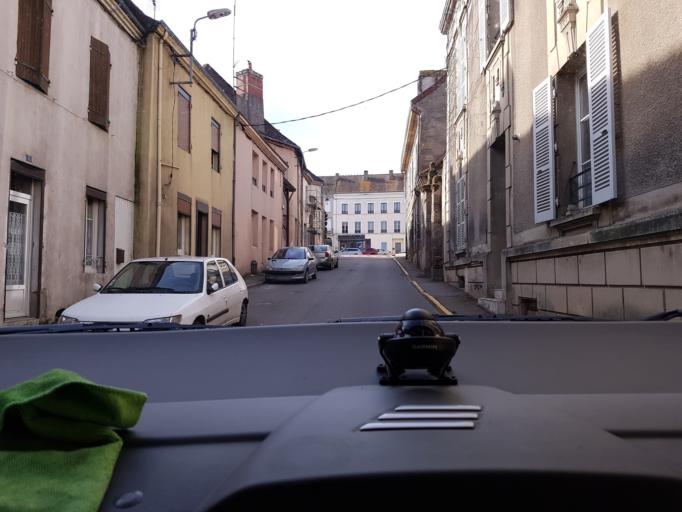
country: FR
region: Bourgogne
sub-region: Departement de Saone-et-Loire
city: Toulon-sur-Arroux
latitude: 46.6941
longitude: 4.1396
